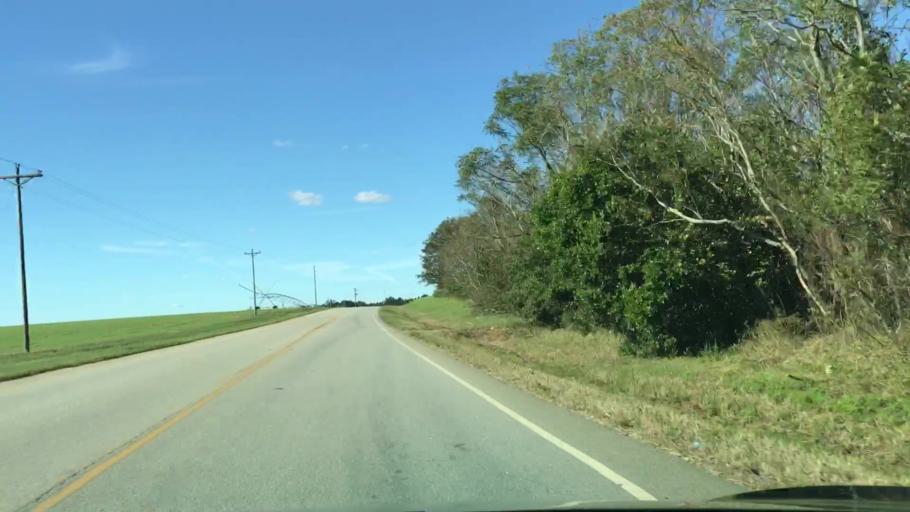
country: US
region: Georgia
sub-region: Jefferson County
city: Louisville
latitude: 33.0764
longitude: -82.4111
